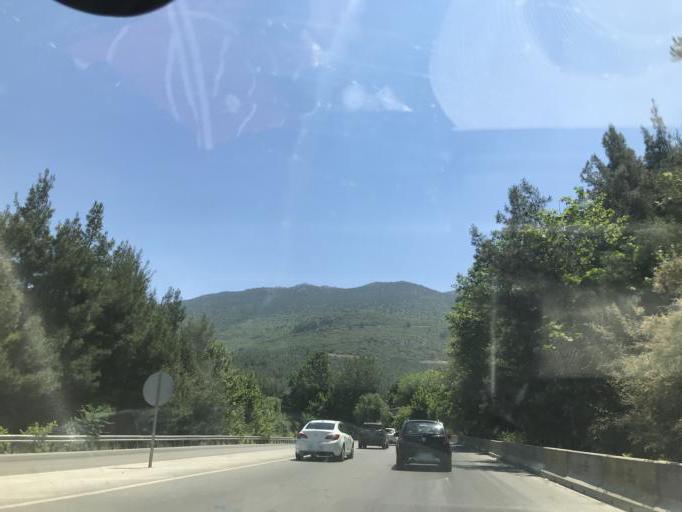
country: TR
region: Denizli
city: Denizli
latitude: 37.7291
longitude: 29.1658
